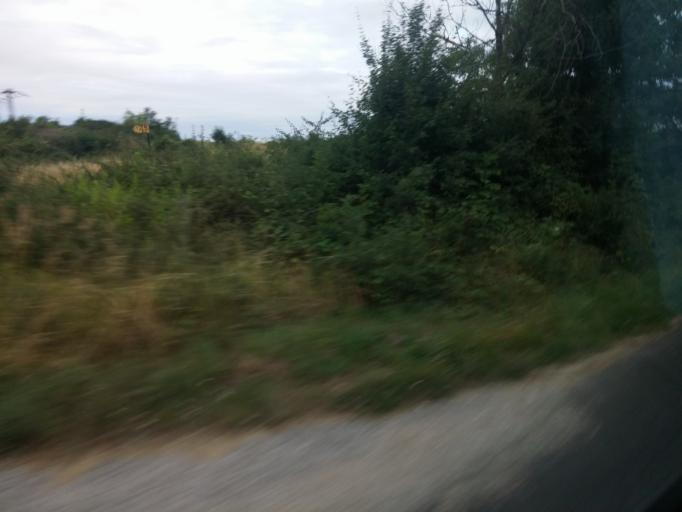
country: HU
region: Fejer
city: Bakonycsernye
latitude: 47.2702
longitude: 18.0542
